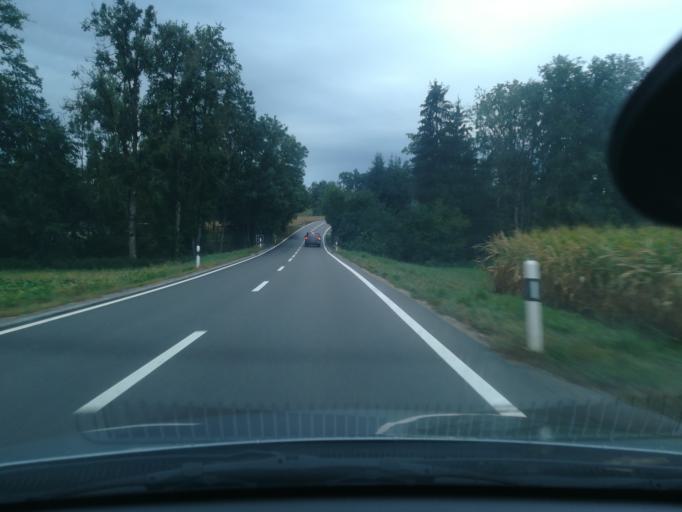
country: CH
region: Thurgau
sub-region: Frauenfeld District
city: Huttwilen
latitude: 47.5991
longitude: 8.8919
